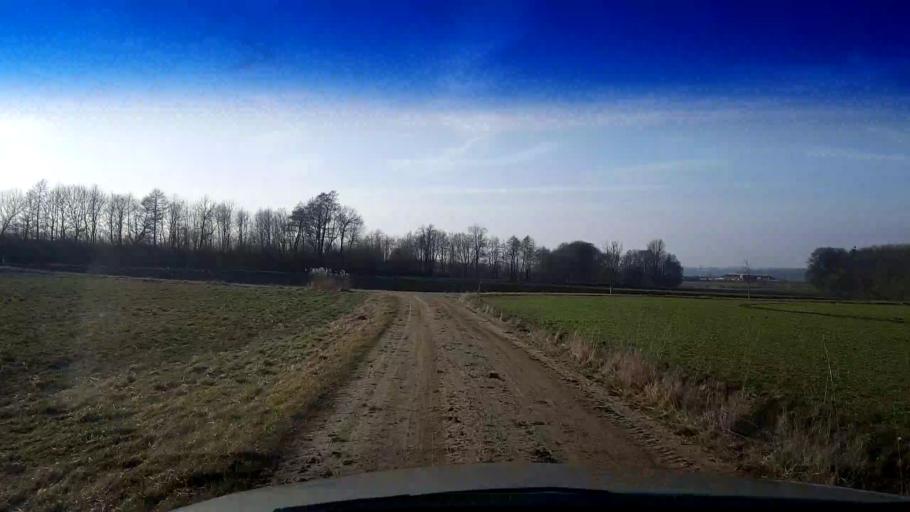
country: DE
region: Bavaria
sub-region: Upper Franconia
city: Schesslitz
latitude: 49.9522
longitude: 11.0315
